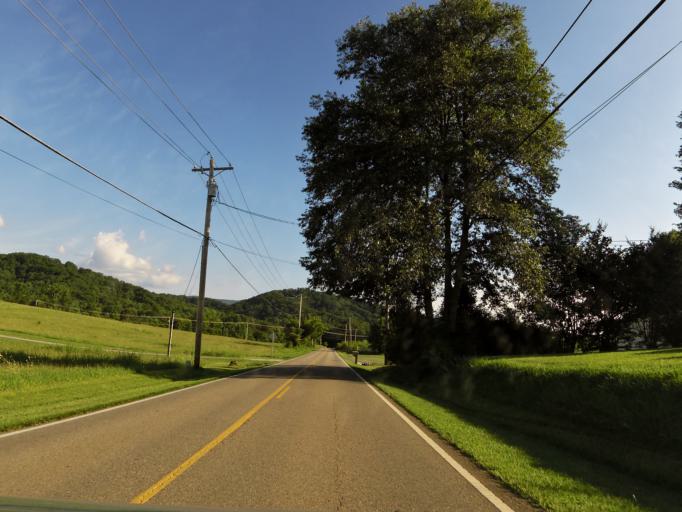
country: US
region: Tennessee
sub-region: Blount County
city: Maryville
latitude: 35.6819
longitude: -83.9739
